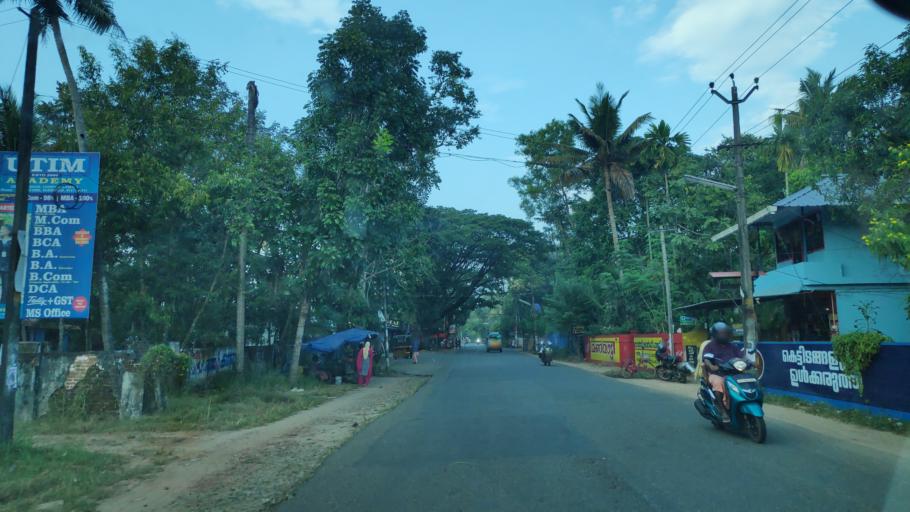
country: IN
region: Kerala
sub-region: Alappuzha
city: Shertallai
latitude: 9.6349
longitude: 76.3714
